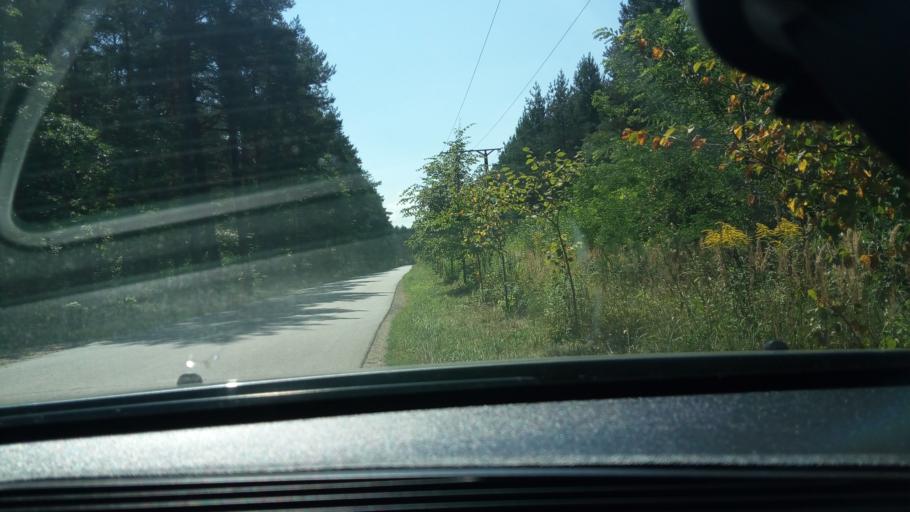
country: PL
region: Lesser Poland Voivodeship
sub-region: Powiat chrzanowski
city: Zarki
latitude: 50.1104
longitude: 19.3701
